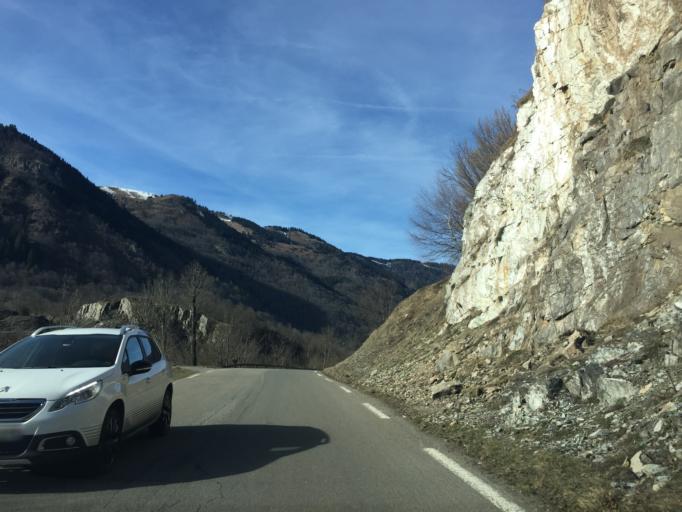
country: FR
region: Midi-Pyrenees
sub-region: Departement des Hautes-Pyrenees
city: Saint-Lary-Soulan
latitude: 42.8080
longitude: 0.4109
